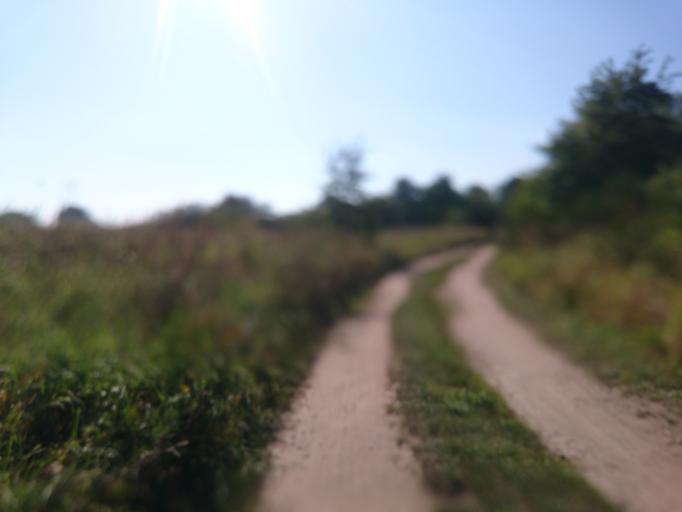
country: DE
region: Mecklenburg-Vorpommern
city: Barth
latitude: 54.3606
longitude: 12.6847
